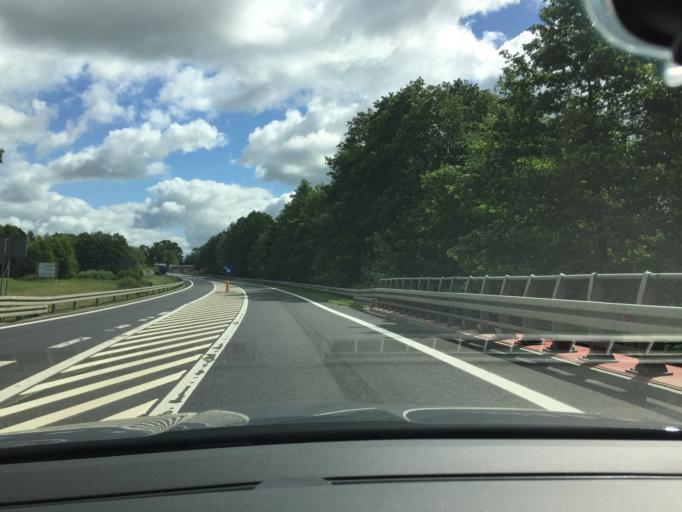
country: PL
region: West Pomeranian Voivodeship
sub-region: Powiat slawienski
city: Darlowo
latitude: 54.2771
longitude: 16.4769
